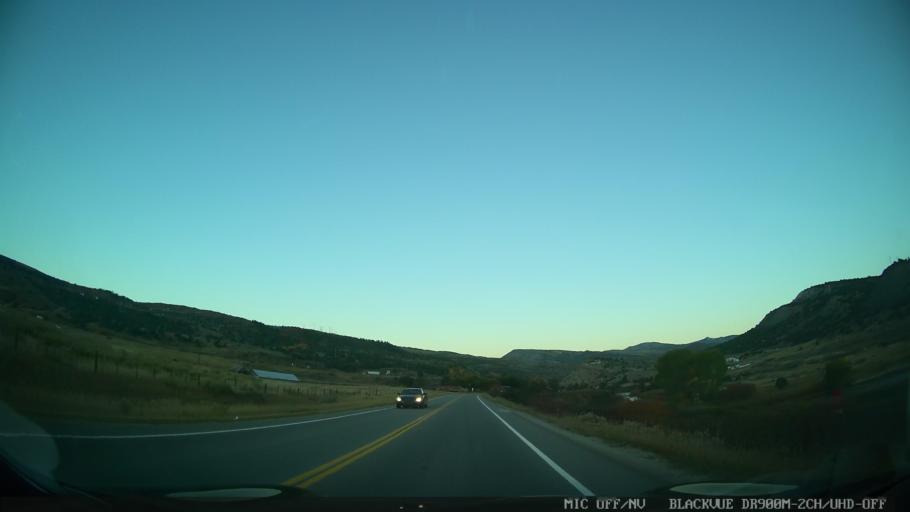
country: US
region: Colorado
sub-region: Eagle County
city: Edwards
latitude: 39.7004
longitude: -106.6707
